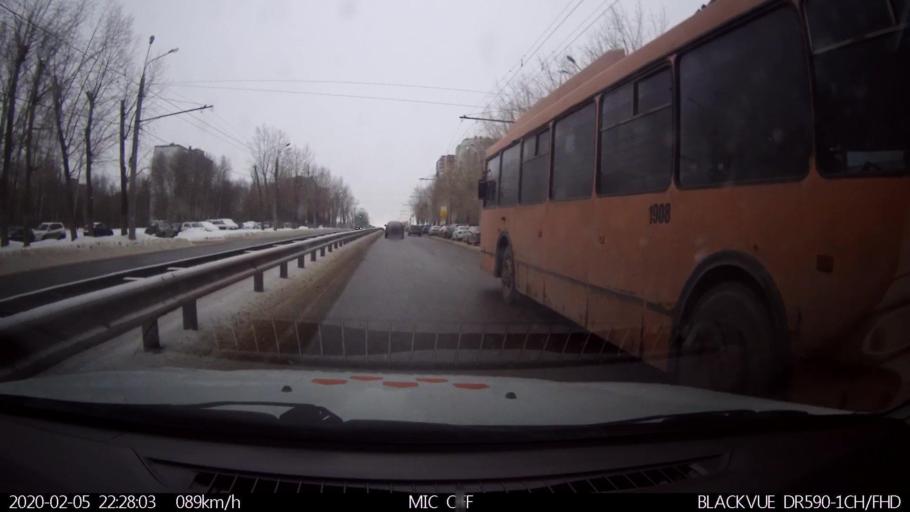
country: RU
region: Nizjnij Novgorod
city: Imeni Stepana Razina
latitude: 54.7603
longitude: 44.1266
